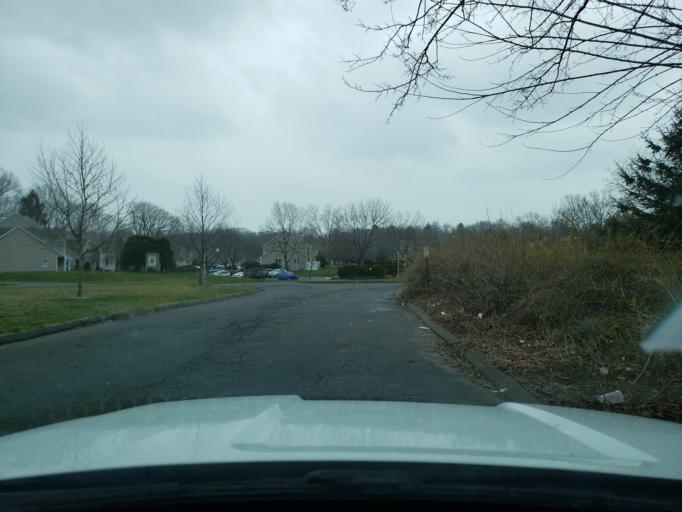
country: US
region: Connecticut
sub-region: Hartford County
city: New Britain
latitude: 41.6744
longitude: -72.7546
